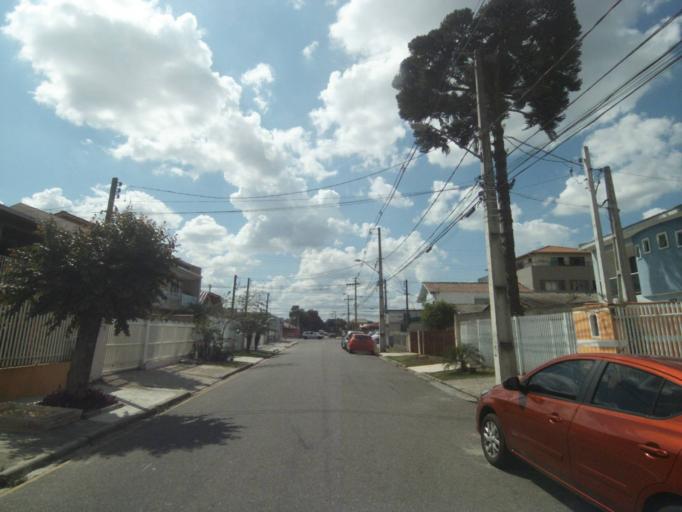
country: BR
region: Parana
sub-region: Sao Jose Dos Pinhais
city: Sao Jose dos Pinhais
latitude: -25.5341
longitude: -49.2645
